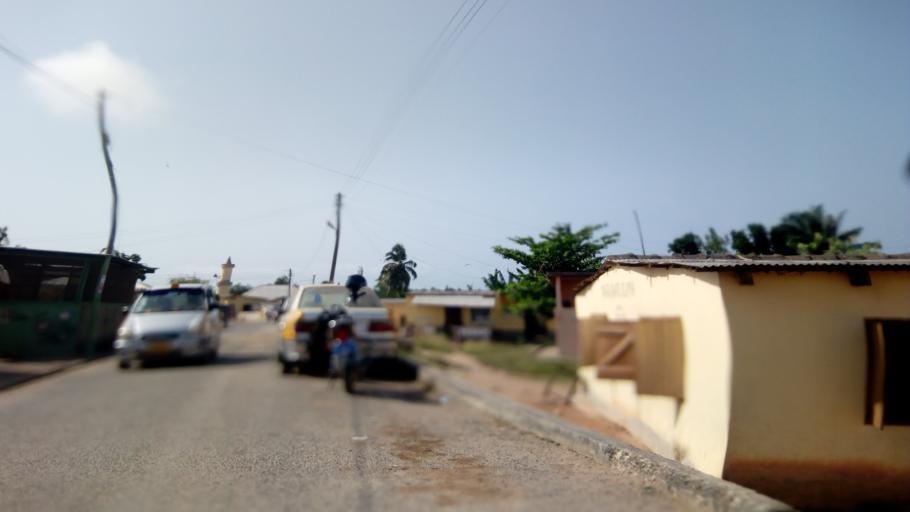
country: GH
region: Central
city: Cape Coast
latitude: 5.1174
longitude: -1.2677
